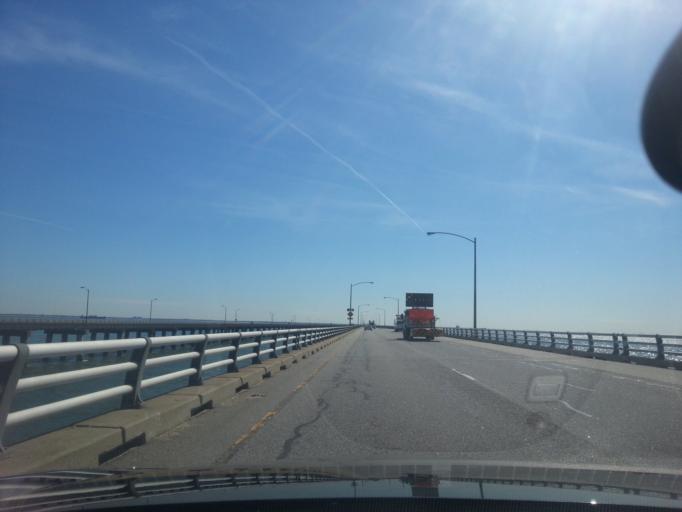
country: US
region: Virginia
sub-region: City of Virginia Beach
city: Virginia Beach
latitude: 37.0084
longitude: -76.0961
